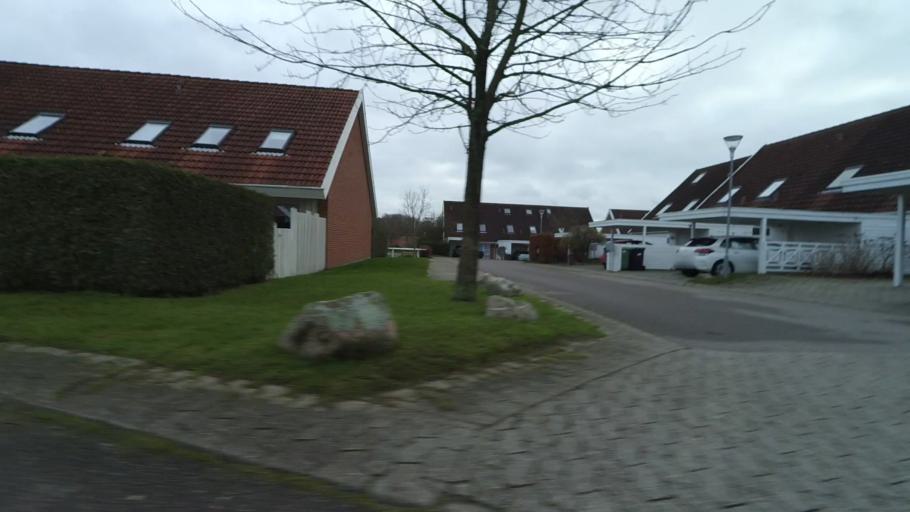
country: DK
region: Central Jutland
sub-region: Arhus Kommune
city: Marslet
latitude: 56.1080
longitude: 10.1759
